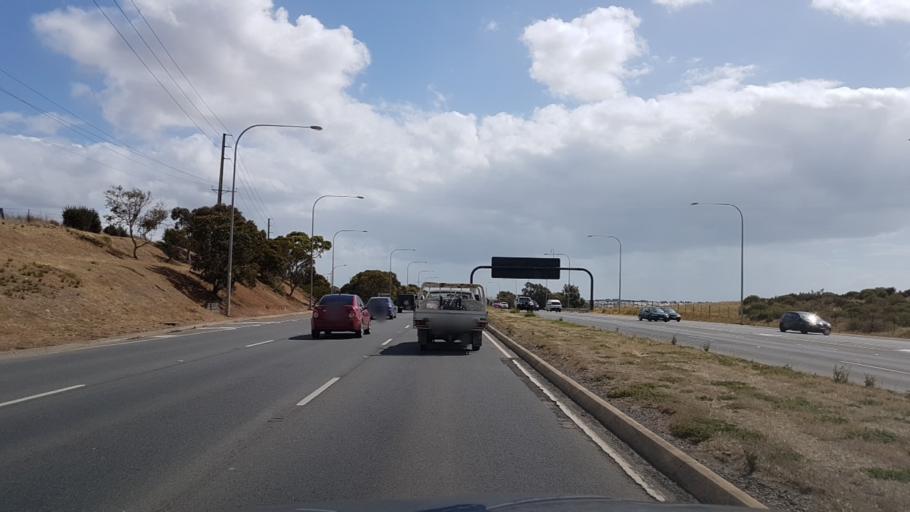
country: AU
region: South Australia
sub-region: Onkaparinga
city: Noarlunga
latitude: -35.1667
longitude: 138.5076
